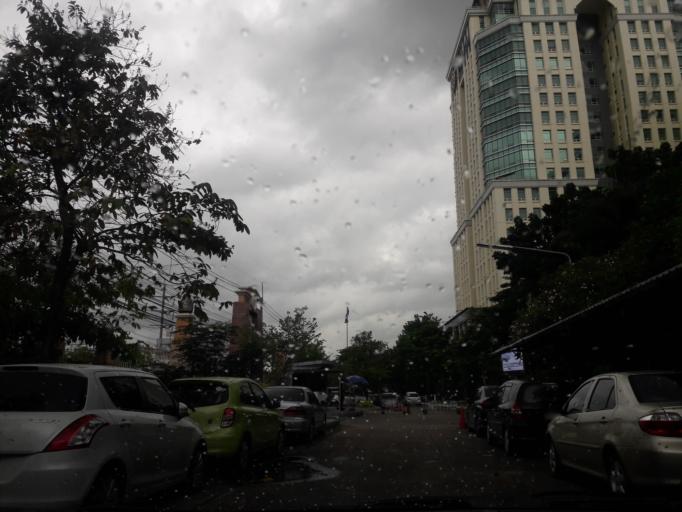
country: TH
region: Bangkok
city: Bang Kapi
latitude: 13.7700
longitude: 100.6529
